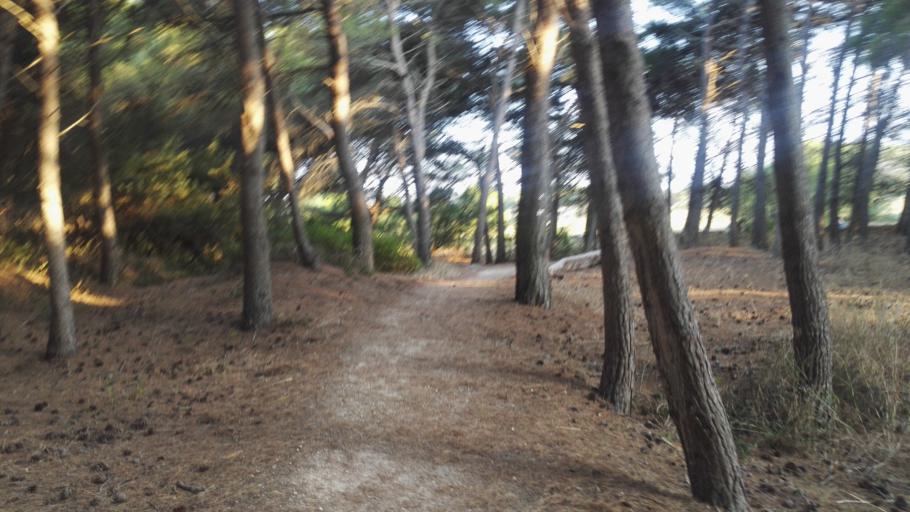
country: IT
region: Apulia
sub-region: Provincia di Lecce
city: Borgagne
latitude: 40.2676
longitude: 18.4334
